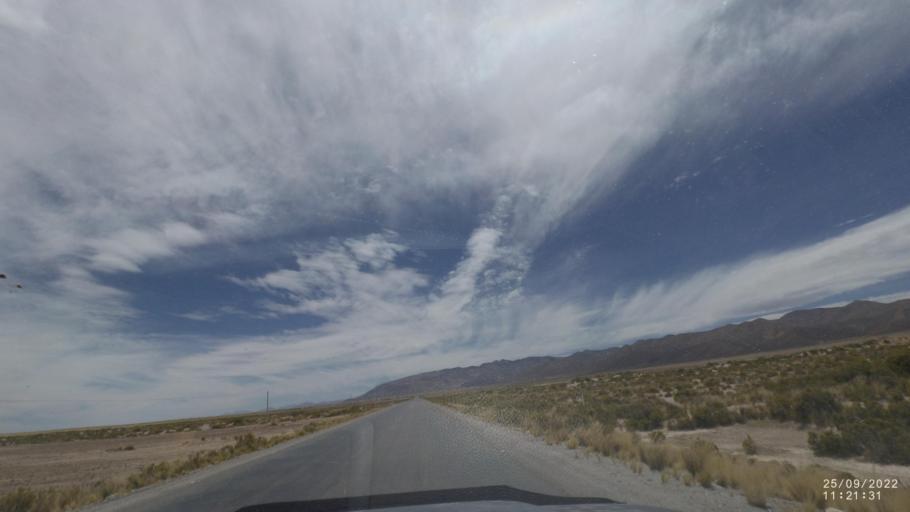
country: BO
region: Oruro
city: Challapata
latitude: -19.1421
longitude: -66.7704
